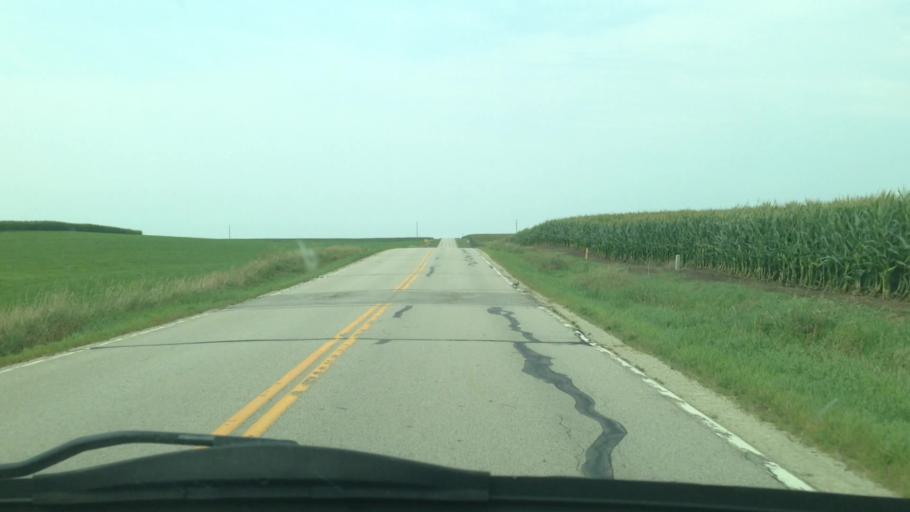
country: US
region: Minnesota
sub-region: Fillmore County
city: Preston
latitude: 43.7770
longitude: -91.9498
